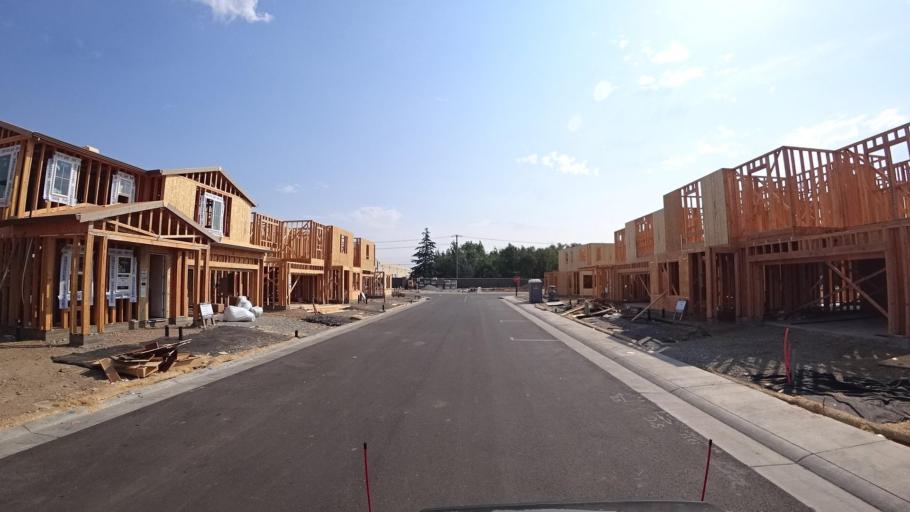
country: US
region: California
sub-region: Placer County
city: Rocklin
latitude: 38.8015
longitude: -121.2170
